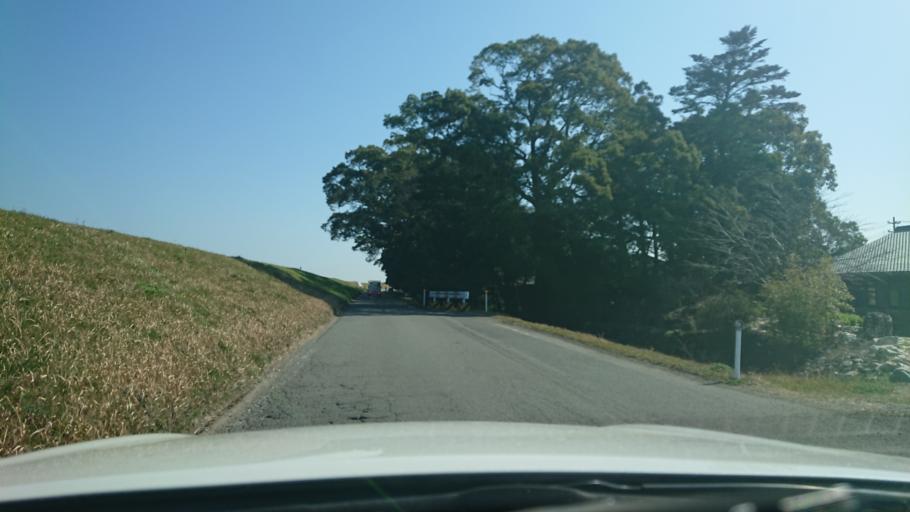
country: JP
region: Tokushima
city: Anan
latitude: 33.9381
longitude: 134.6152
